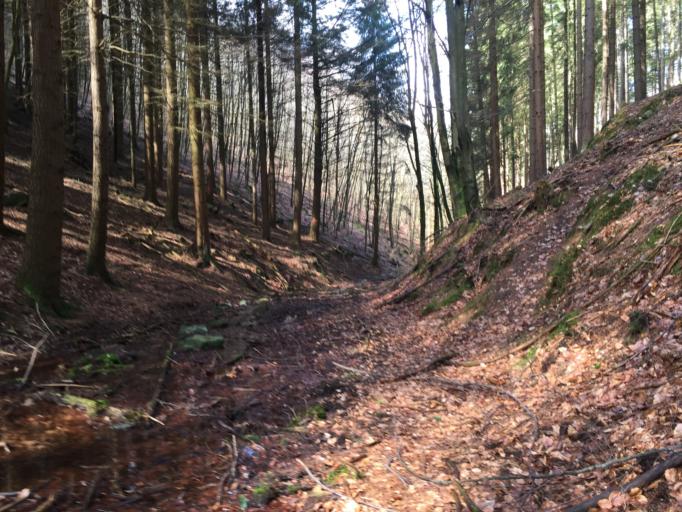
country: DE
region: Rheinland-Pfalz
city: Elmstein
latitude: 49.3916
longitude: 7.9420
